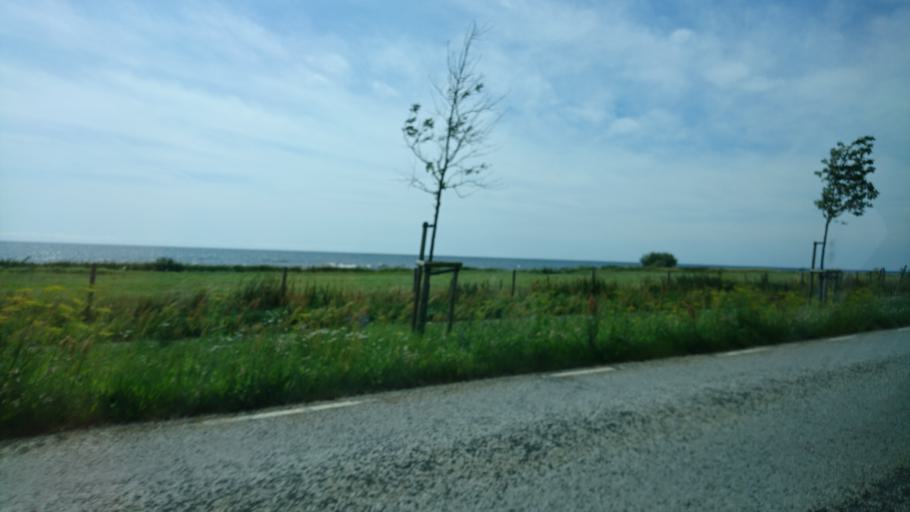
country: SE
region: Skane
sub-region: Skurups Kommun
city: Skivarp
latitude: 55.3876
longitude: 13.5312
